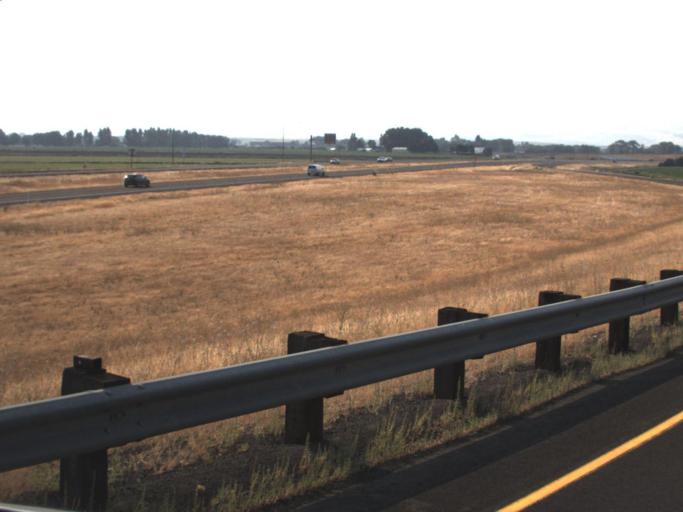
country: US
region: Washington
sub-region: Kittitas County
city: Ellensburg
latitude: 46.9670
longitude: -120.5102
